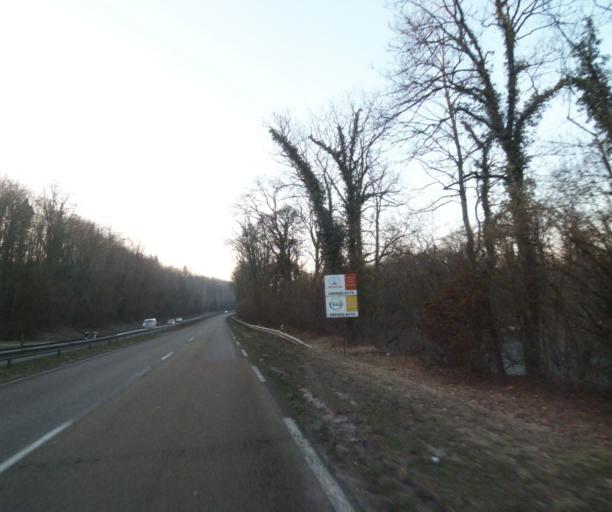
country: FR
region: Lorraine
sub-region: Departement de la Meuse
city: Ancerville
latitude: 48.6109
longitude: 5.0068
